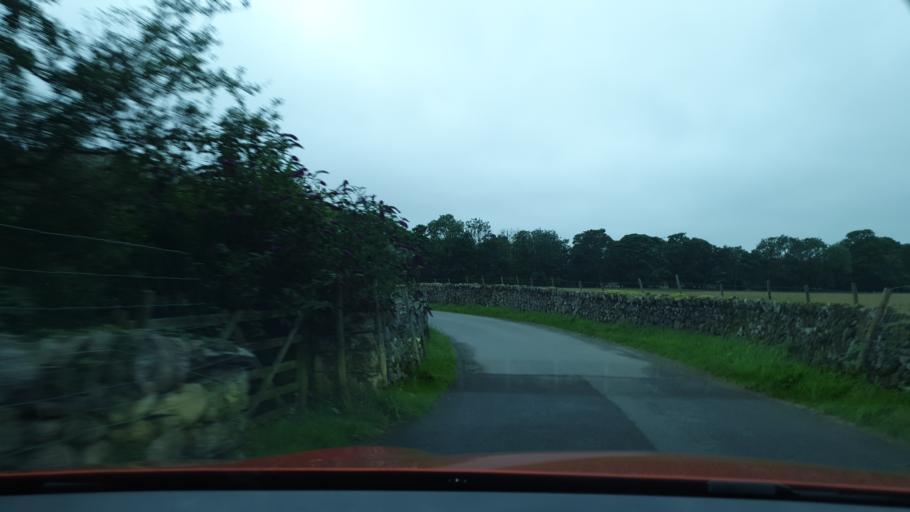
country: GB
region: England
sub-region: Cumbria
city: Seascale
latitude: 54.3858
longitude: -3.3121
